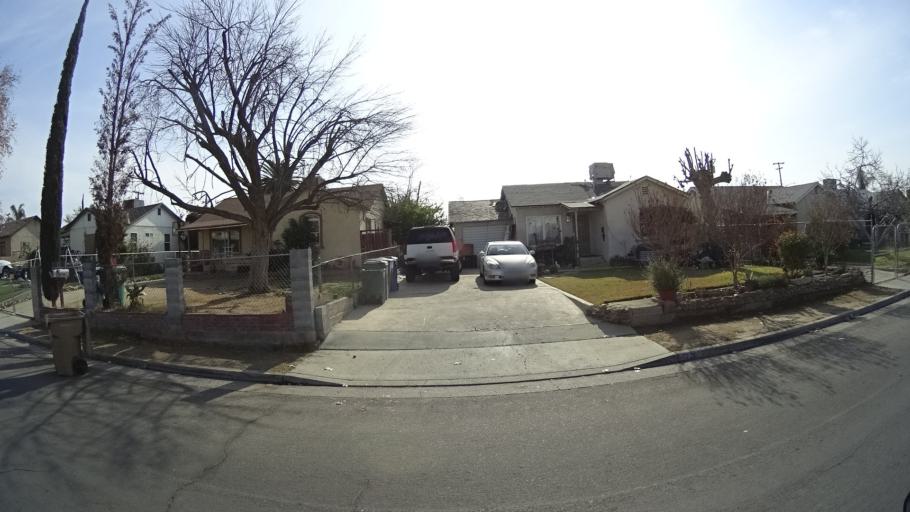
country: US
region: California
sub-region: Kern County
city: Bakersfield
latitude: 35.3957
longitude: -118.9839
